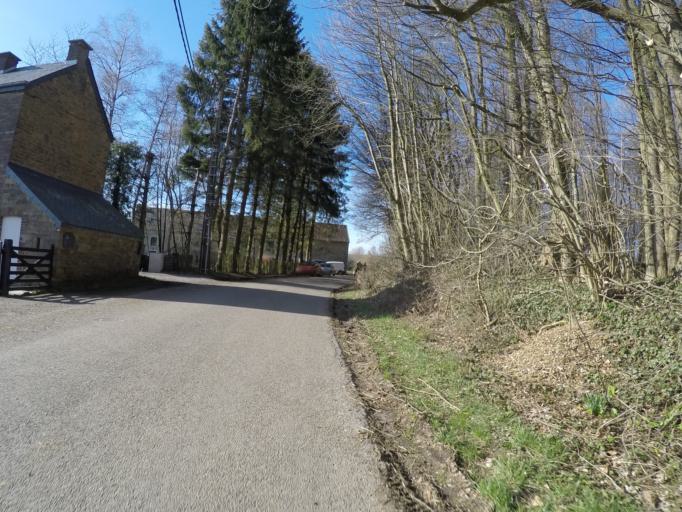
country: BE
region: Wallonia
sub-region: Province de Namur
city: Gesves
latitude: 50.3600
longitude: 5.0818
